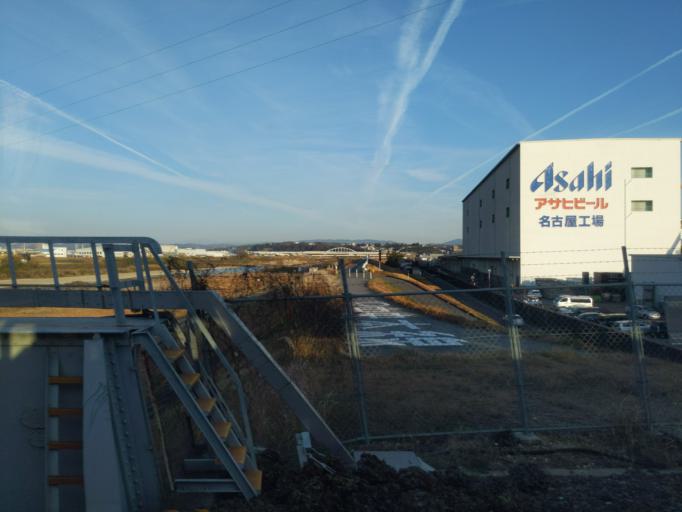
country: JP
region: Aichi
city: Kasugai
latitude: 35.2159
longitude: 136.9533
